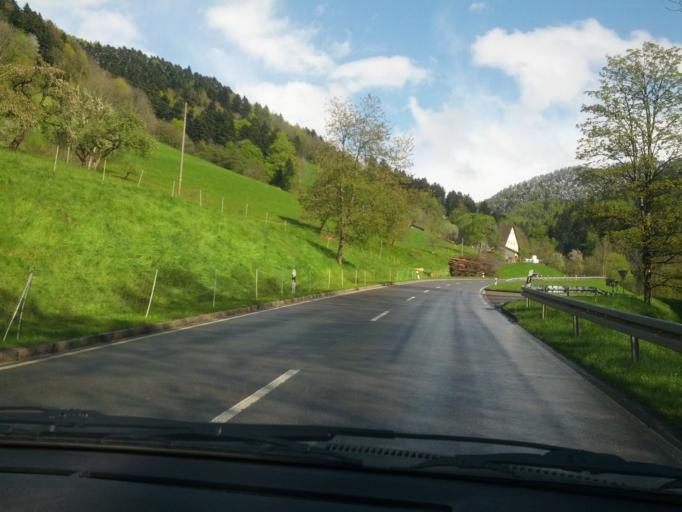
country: DE
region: Baden-Wuerttemberg
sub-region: Freiburg Region
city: Glottertal
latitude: 48.0369
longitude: 7.9879
